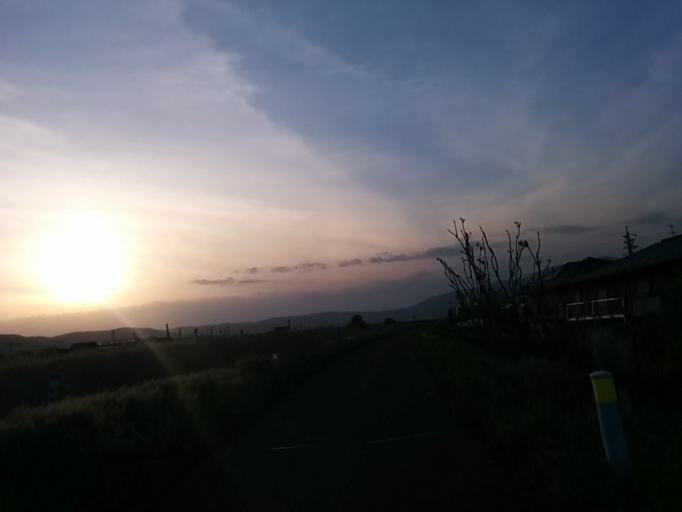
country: JP
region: Nagano
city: Suwa
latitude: 36.0291
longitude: 138.1123
